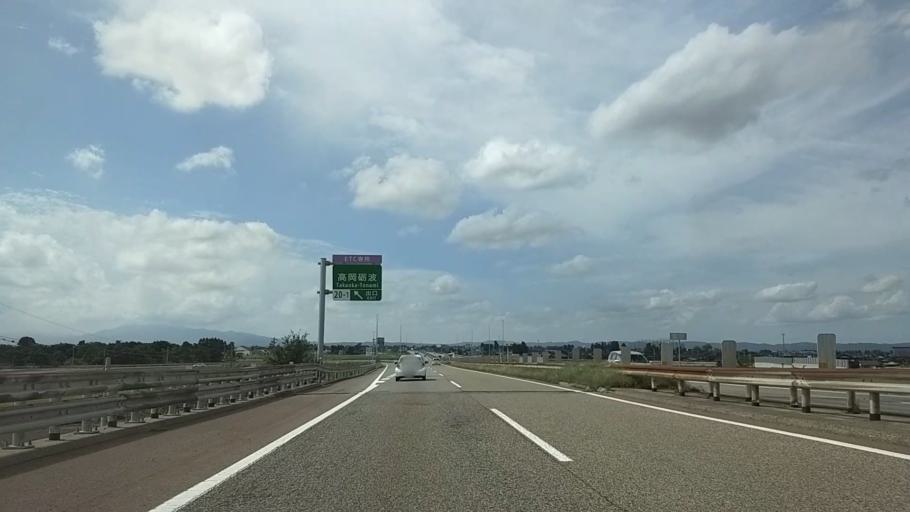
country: JP
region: Toyama
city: Takaoka
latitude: 36.6563
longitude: 137.0041
